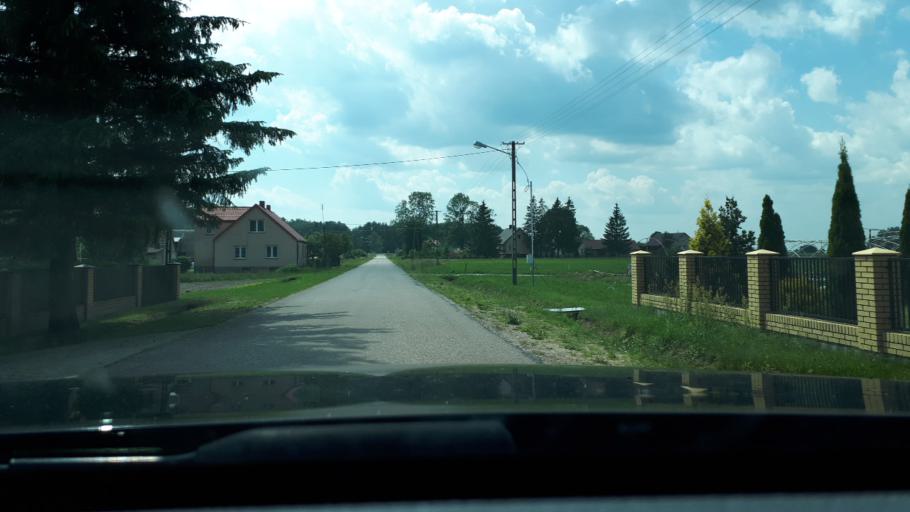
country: PL
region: Podlasie
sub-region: Powiat bialostocki
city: Lapy
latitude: 53.1060
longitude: 22.8710
